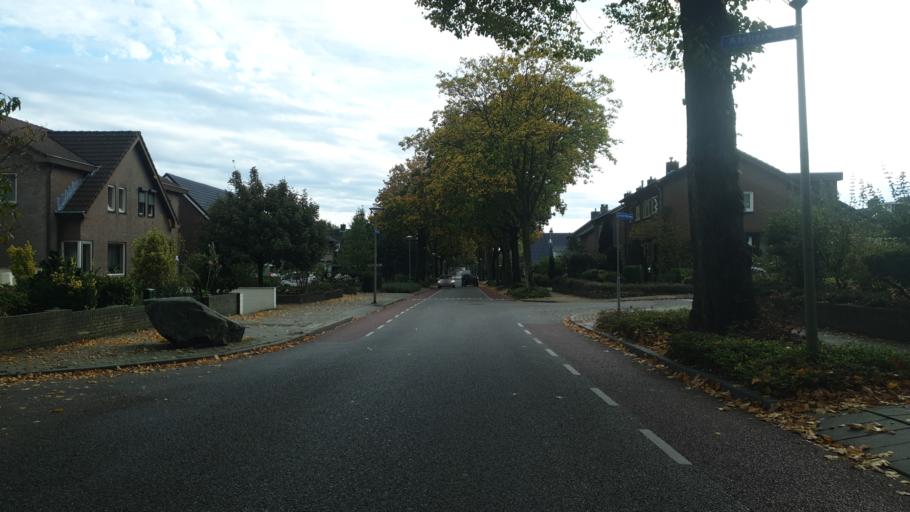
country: NL
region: Gelderland
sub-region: Gemeente Groesbeek
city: Groesbeek
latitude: 51.7752
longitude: 5.9415
